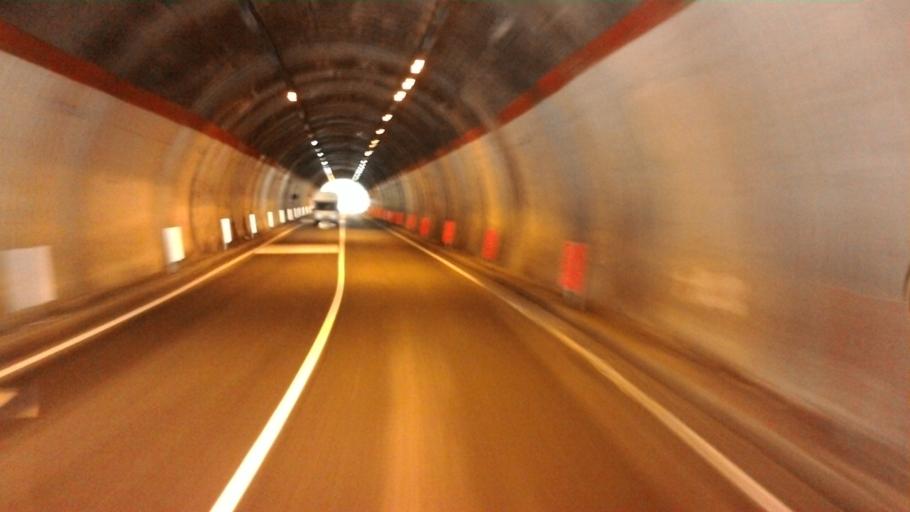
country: IT
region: Aosta Valley
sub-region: Valle d'Aosta
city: Introd
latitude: 45.7059
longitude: 7.1776
